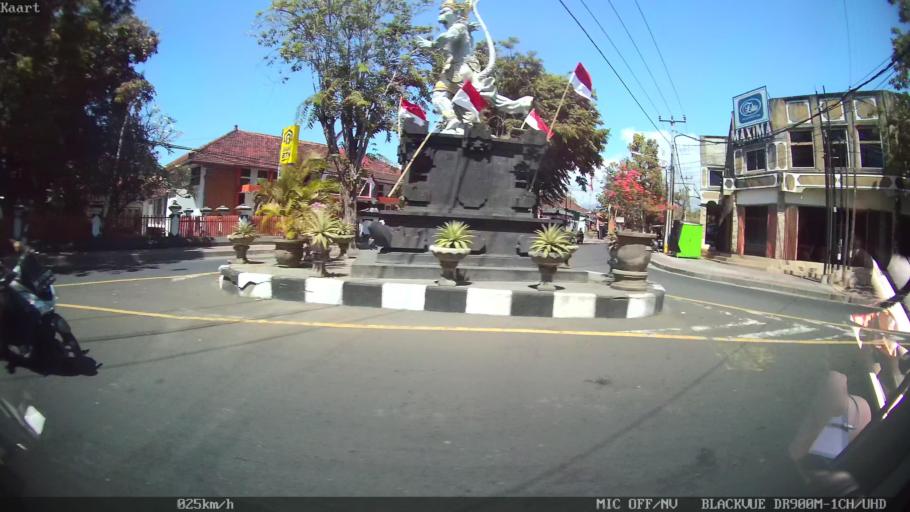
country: ID
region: Bali
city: Banjar Kampungkajanan
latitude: -8.1089
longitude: 115.0910
